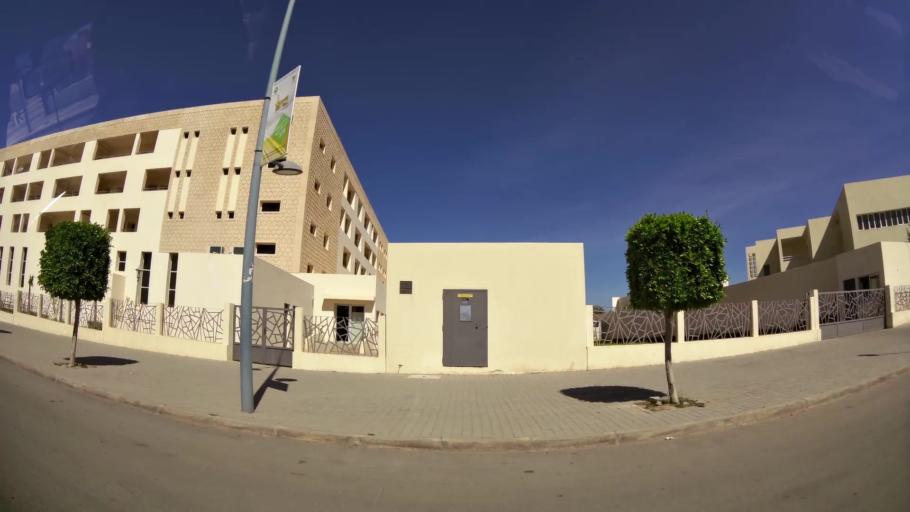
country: MA
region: Oriental
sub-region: Oujda-Angad
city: Oujda
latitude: 34.6600
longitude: -1.9121
